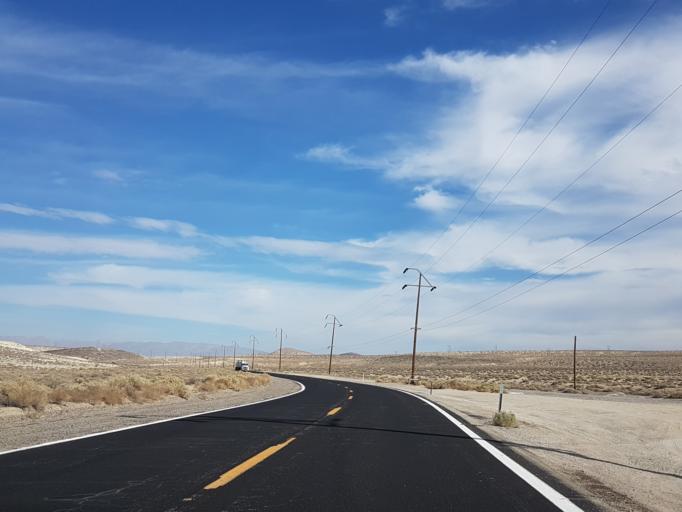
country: US
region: California
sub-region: San Bernardino County
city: Searles Valley
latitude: 35.6493
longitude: -117.4753
